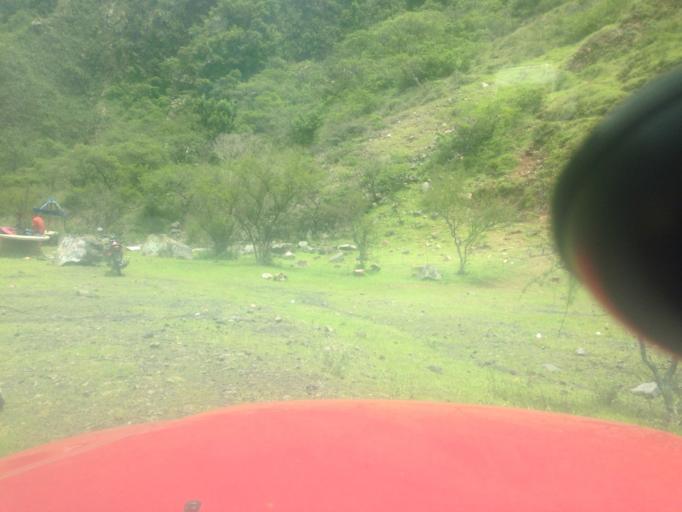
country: MX
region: Nayarit
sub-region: Ahuacatlan
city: Ahuacatlan
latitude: 21.1150
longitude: -104.5044
